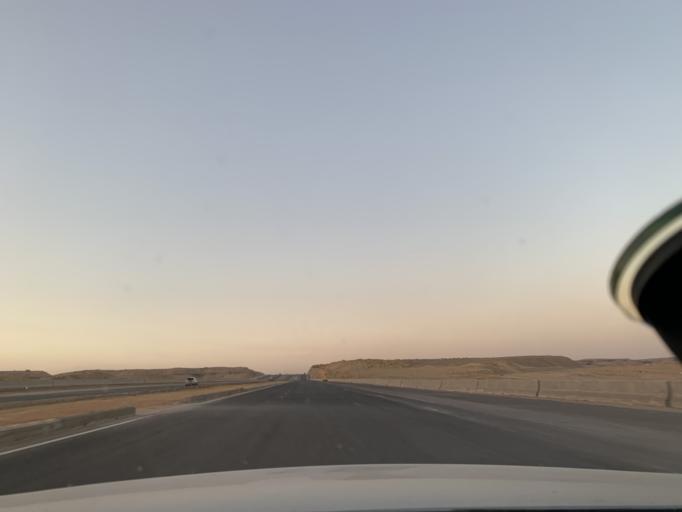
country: EG
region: Muhafazat al Qahirah
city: Halwan
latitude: 29.9410
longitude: 31.5318
